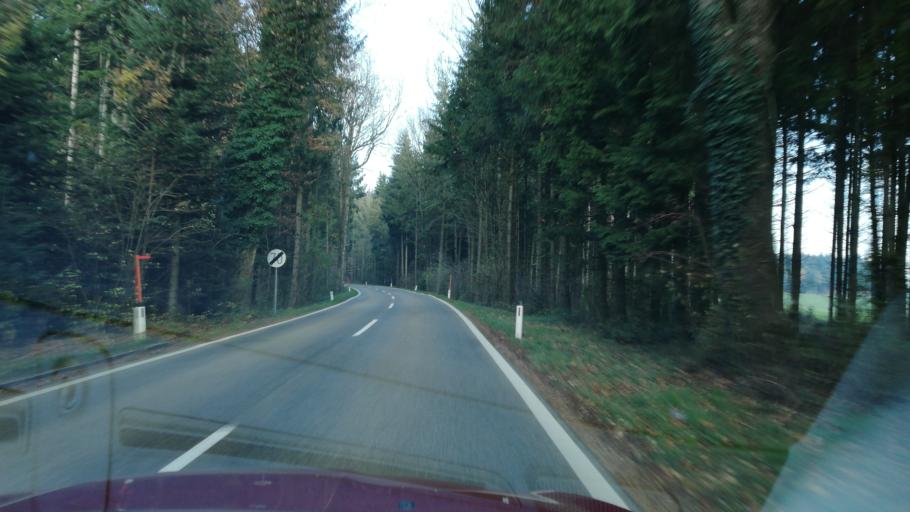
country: AT
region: Upper Austria
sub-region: Wels-Land
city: Thalheim bei Wels
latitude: 48.1337
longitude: 14.0627
